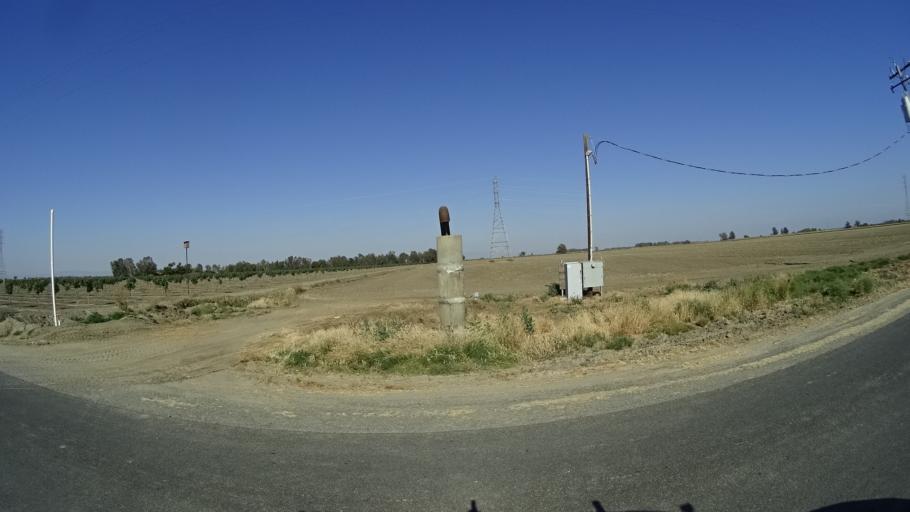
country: US
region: California
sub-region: Fresno County
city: Riverdale
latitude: 36.3549
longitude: -119.8872
